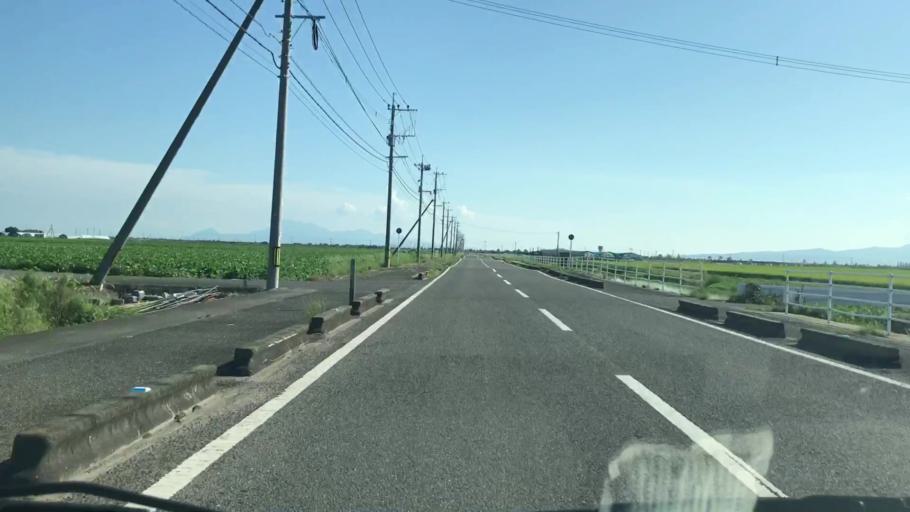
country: JP
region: Saga Prefecture
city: Okawa
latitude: 33.1724
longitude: 130.3109
